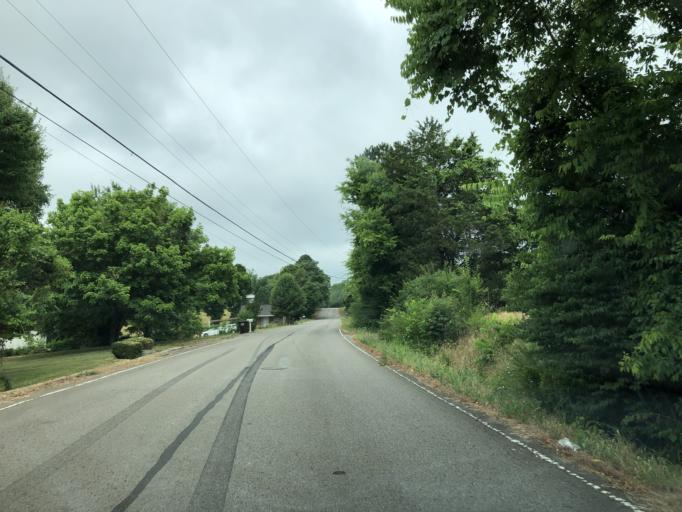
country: US
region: Tennessee
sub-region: Davidson County
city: Goodlettsville
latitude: 36.2898
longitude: -86.7491
